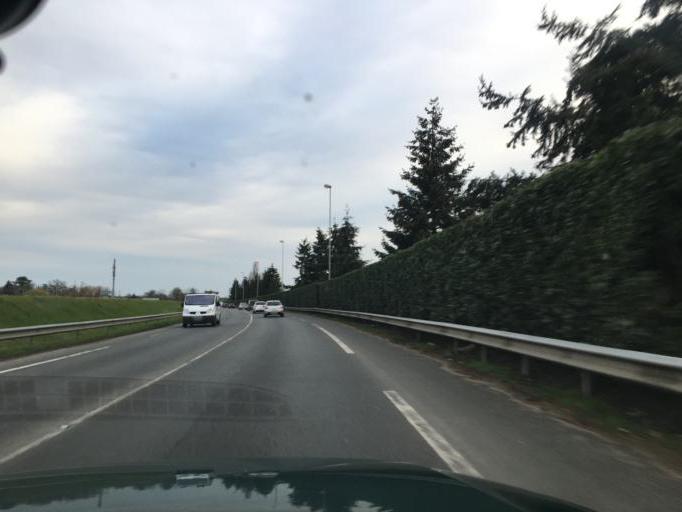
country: FR
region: Centre
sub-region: Departement du Loiret
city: Saint-Jean-le-Blanc
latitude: 47.8821
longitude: 1.9249
